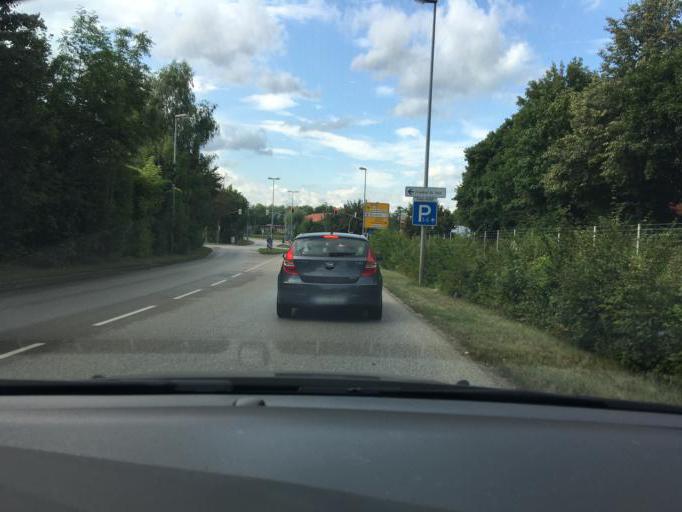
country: DE
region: Bavaria
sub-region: Upper Bavaria
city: Erding
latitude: 48.3092
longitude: 11.9182
